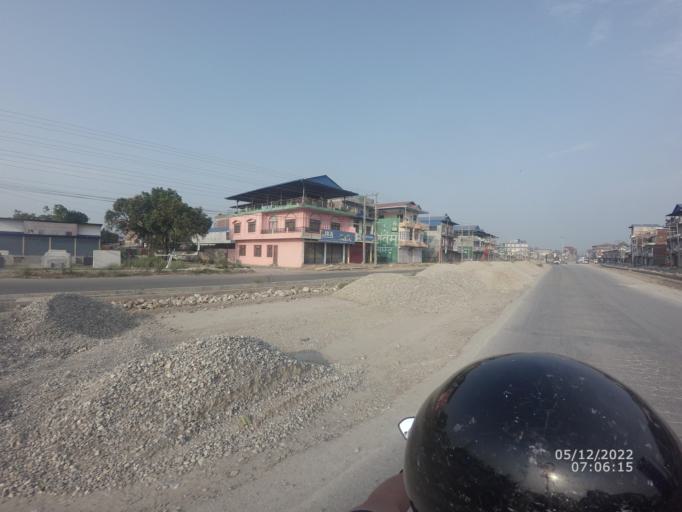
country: NP
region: Central Region
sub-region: Narayani Zone
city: Bharatpur
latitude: 27.6704
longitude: 84.4408
